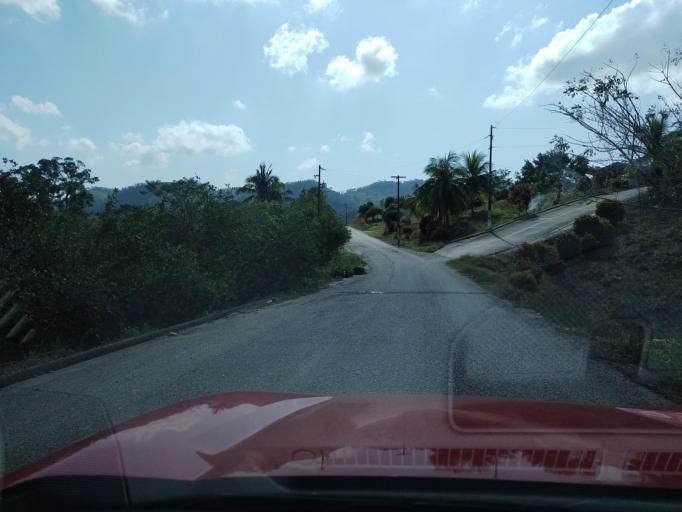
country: MX
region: Veracruz
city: Agua Dulce
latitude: 20.3061
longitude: -97.1740
